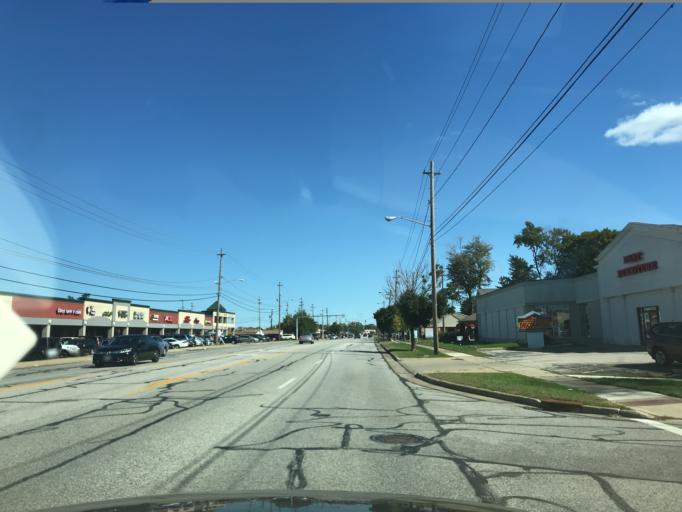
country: US
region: Ohio
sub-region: Lake County
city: Kirtland
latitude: 41.6555
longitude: -81.3729
